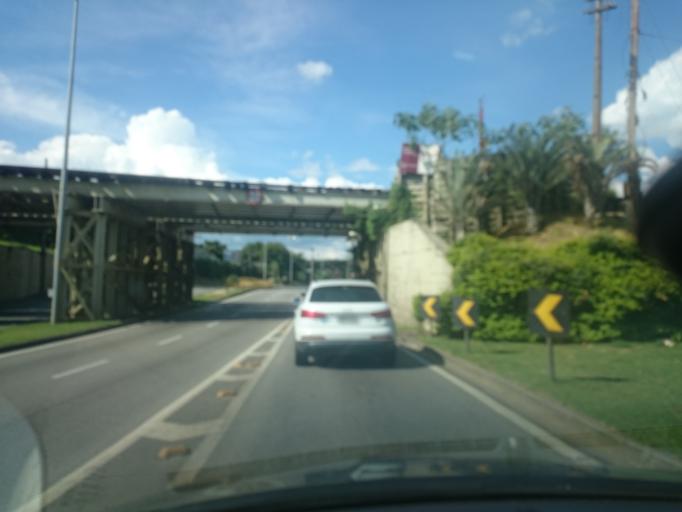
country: BR
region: Sao Paulo
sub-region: Sorocaba
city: Sorocaba
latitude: -23.4971
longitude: -47.4509
